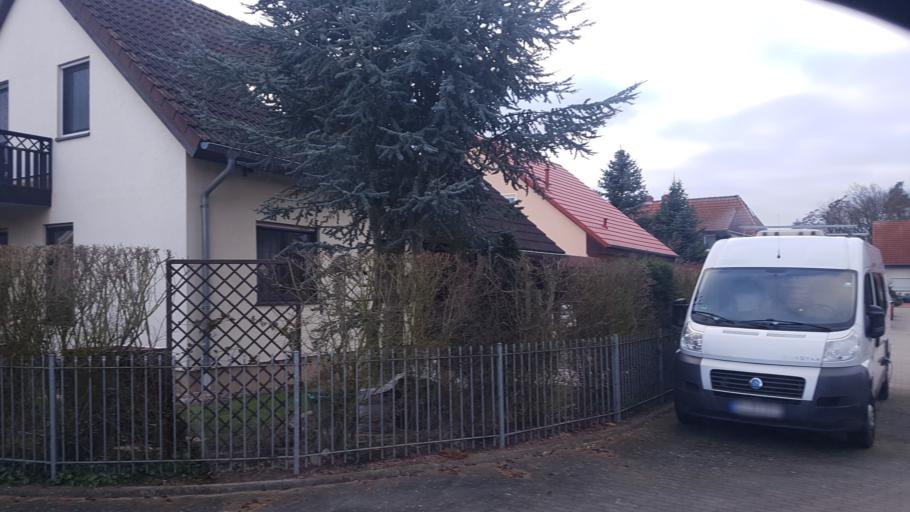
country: DE
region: Brandenburg
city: Ludwigsfelde
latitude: 52.3400
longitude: 13.2297
